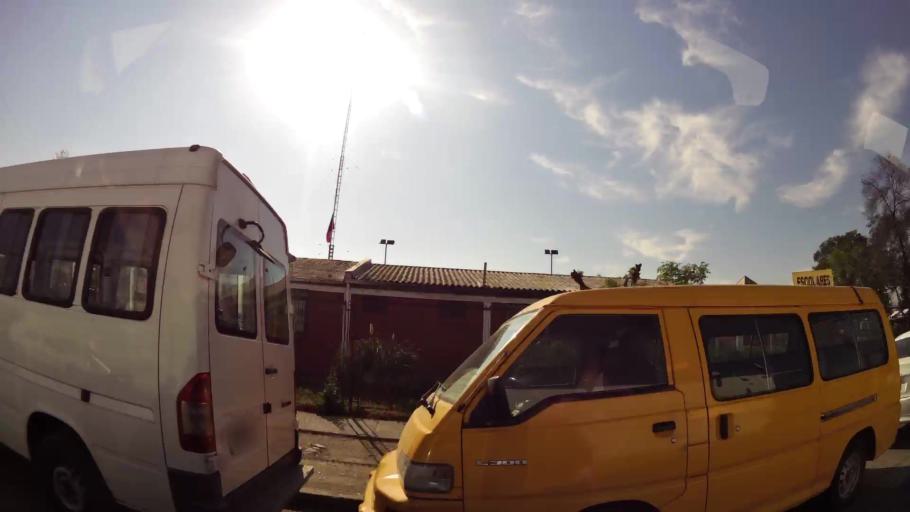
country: CL
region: Santiago Metropolitan
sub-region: Provincia de Santiago
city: La Pintana
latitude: -33.5582
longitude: -70.5993
